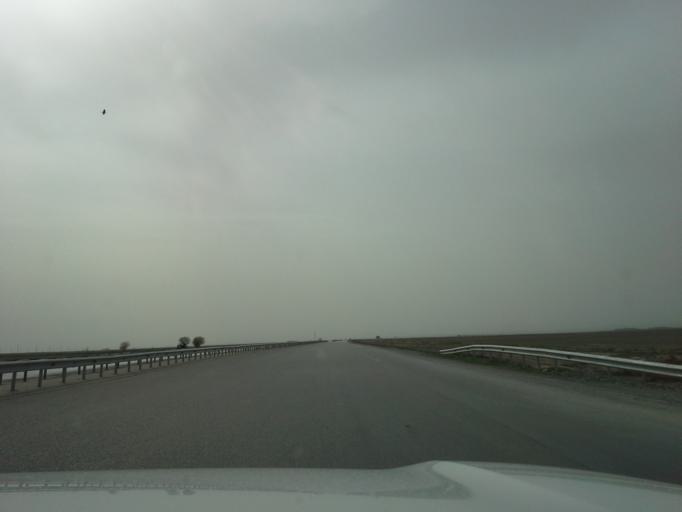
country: TM
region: Ahal
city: Kaka
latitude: 37.4678
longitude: 59.5015
